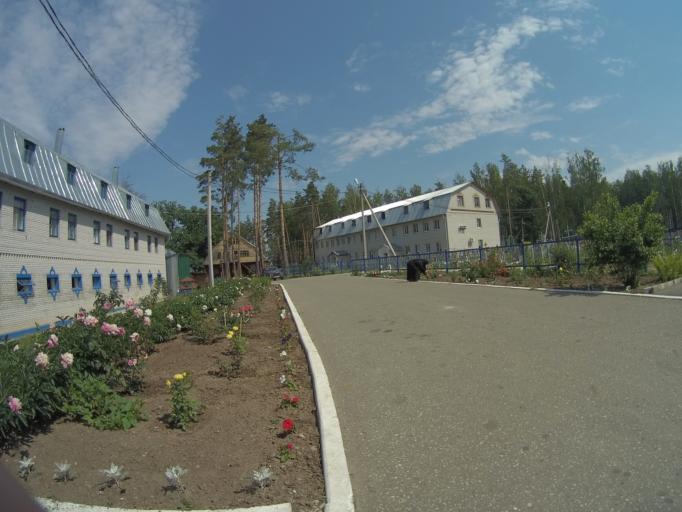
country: RU
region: Vladimir
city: Sudogda
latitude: 56.1481
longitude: 40.8184
